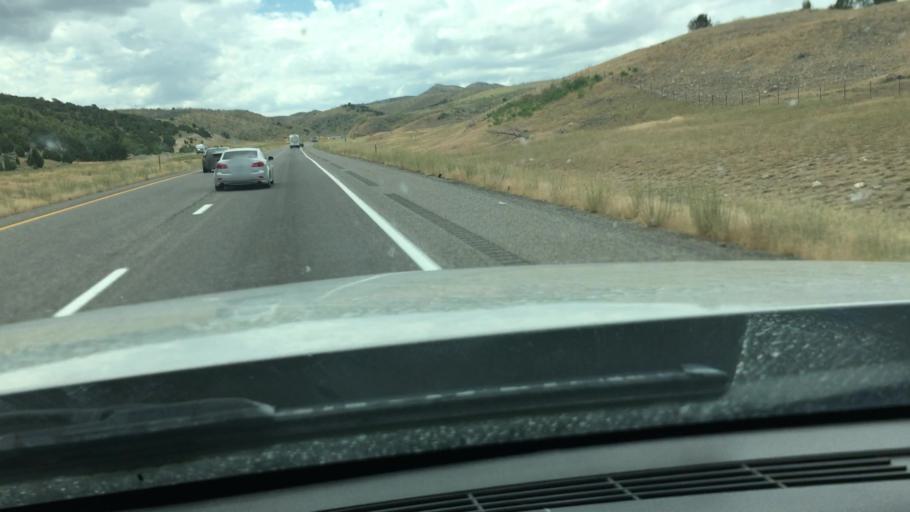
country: US
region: Utah
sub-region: Millard County
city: Fillmore
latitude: 38.7123
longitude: -112.5996
